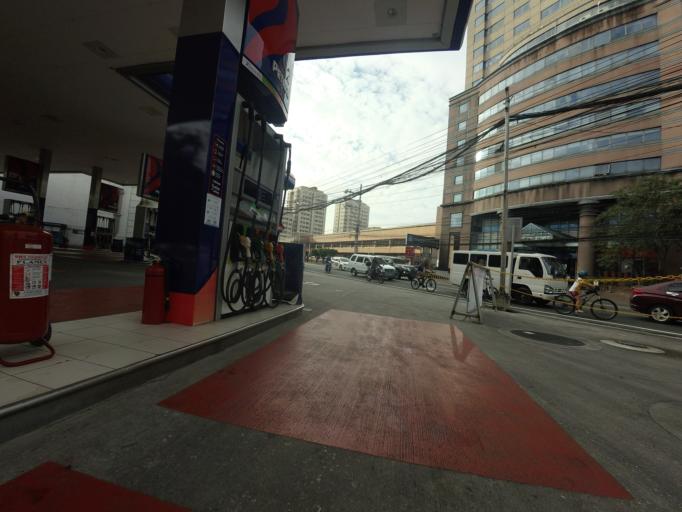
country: PH
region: Metro Manila
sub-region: Mandaluyong
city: Mandaluyong City
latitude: 14.5873
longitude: 121.0473
